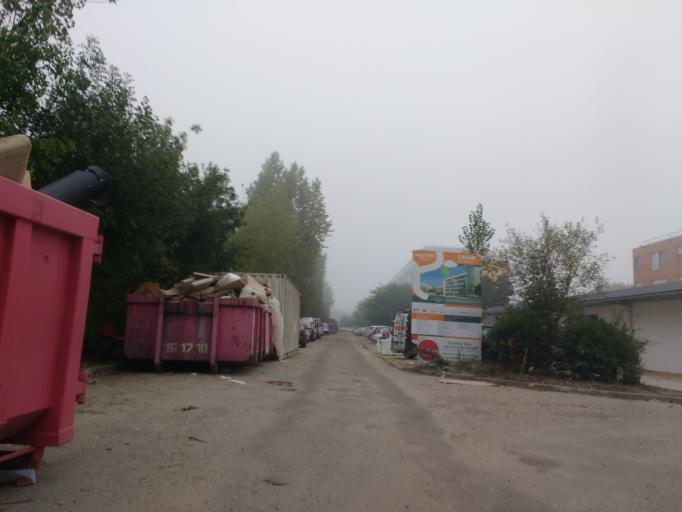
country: FR
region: Aquitaine
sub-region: Departement de la Gironde
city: Talence
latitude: 44.8020
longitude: -0.6028
